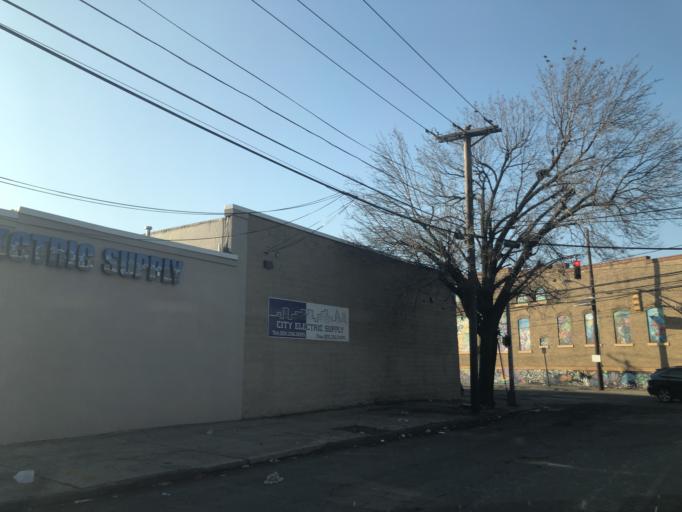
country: US
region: New Jersey
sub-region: Hudson County
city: Jersey City
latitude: 40.7165
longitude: -74.0621
